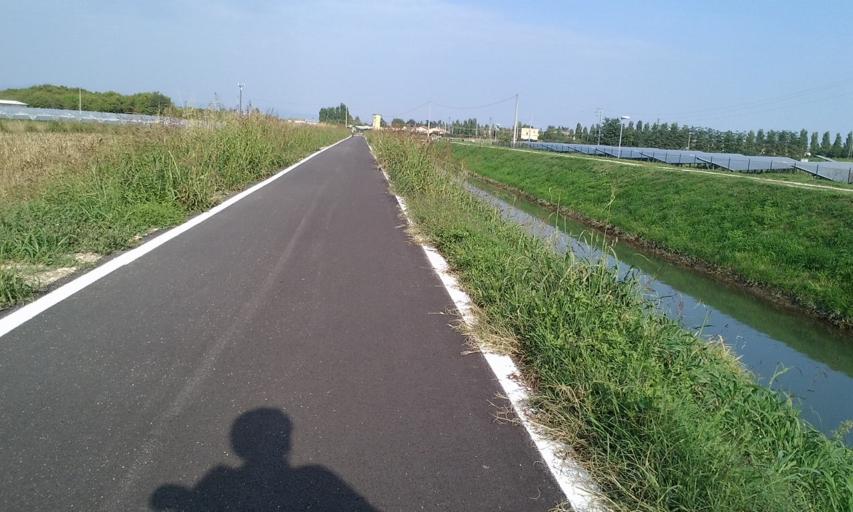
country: IT
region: Veneto
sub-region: Provincia di Verona
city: Raldon
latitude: 45.3538
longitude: 11.0354
